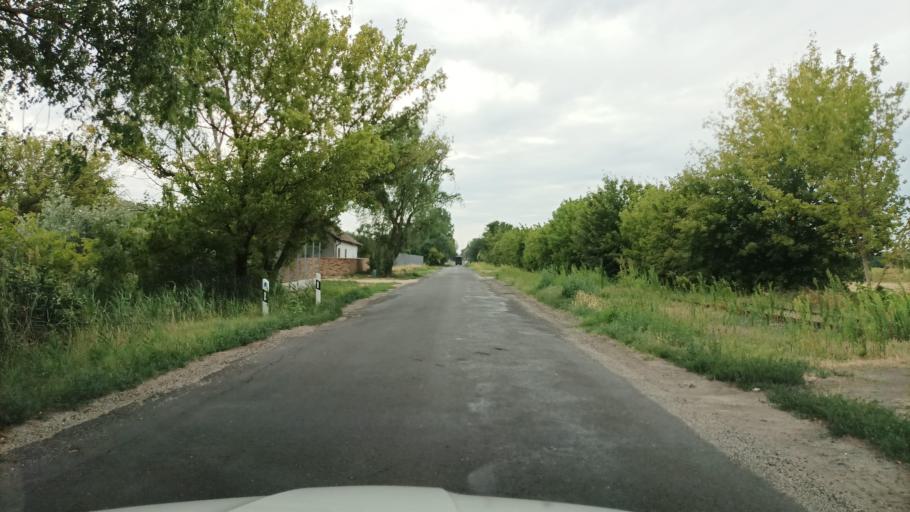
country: HU
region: Pest
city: Taborfalva
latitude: 47.0862
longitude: 19.4565
